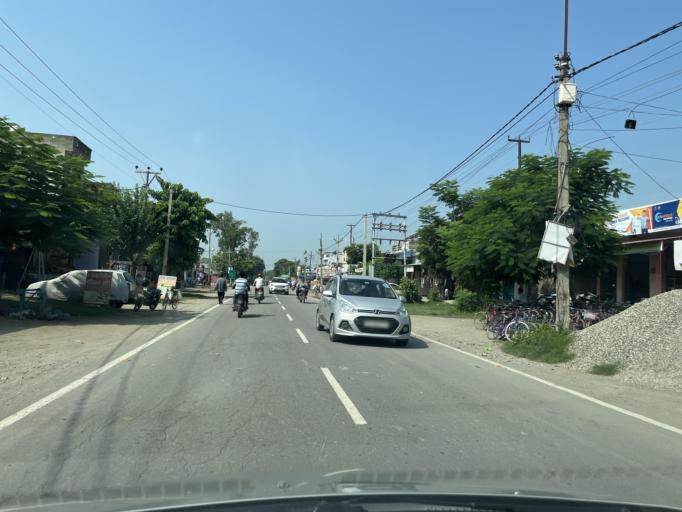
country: IN
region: Uttarakhand
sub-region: Udham Singh Nagar
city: Bazpur
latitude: 29.2057
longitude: 79.2100
